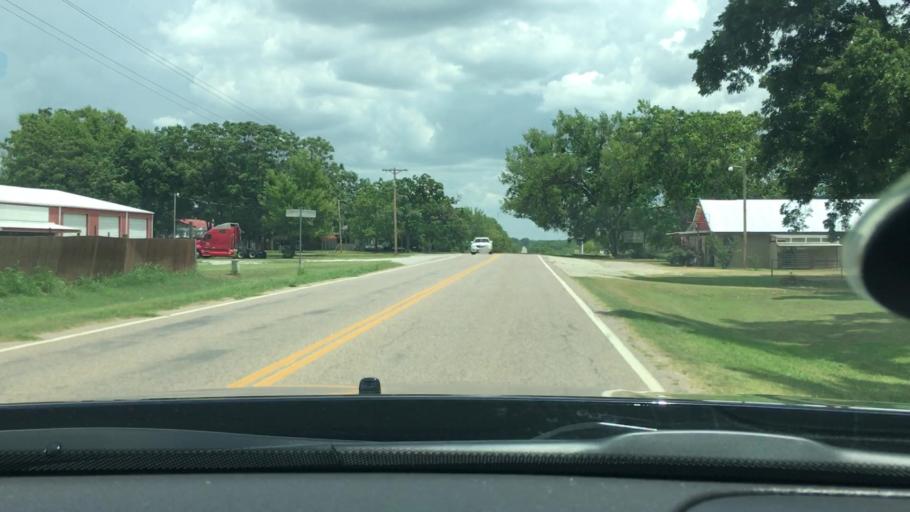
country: US
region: Texas
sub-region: Grayson County
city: Sherwood Shores
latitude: 33.9836
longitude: -96.9100
